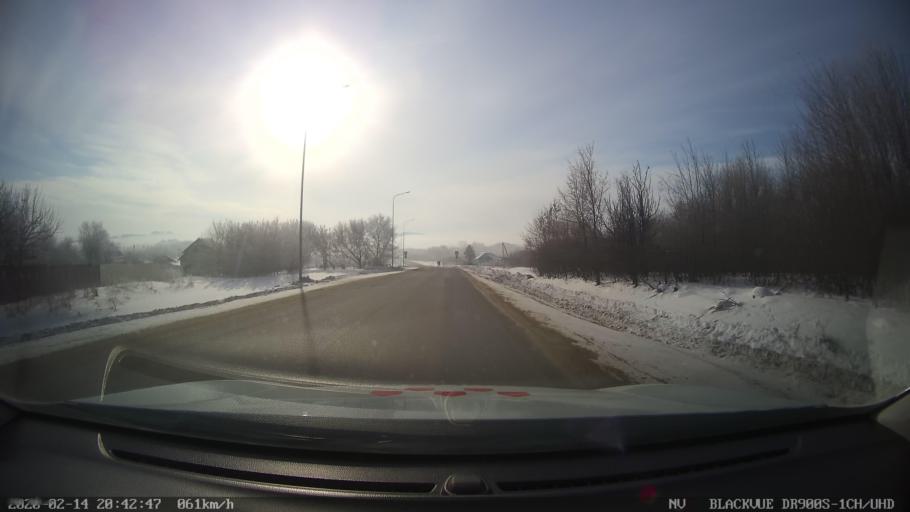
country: RU
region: Tatarstan
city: Kuybyshevskiy Zaton
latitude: 55.3143
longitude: 49.1445
